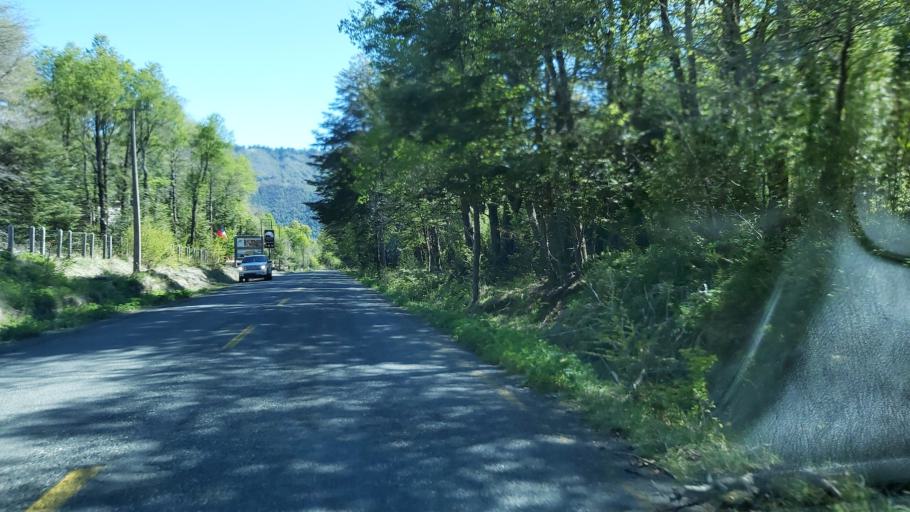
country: CL
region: Araucania
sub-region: Provincia de Cautin
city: Vilcun
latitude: -38.4768
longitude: -71.5326
